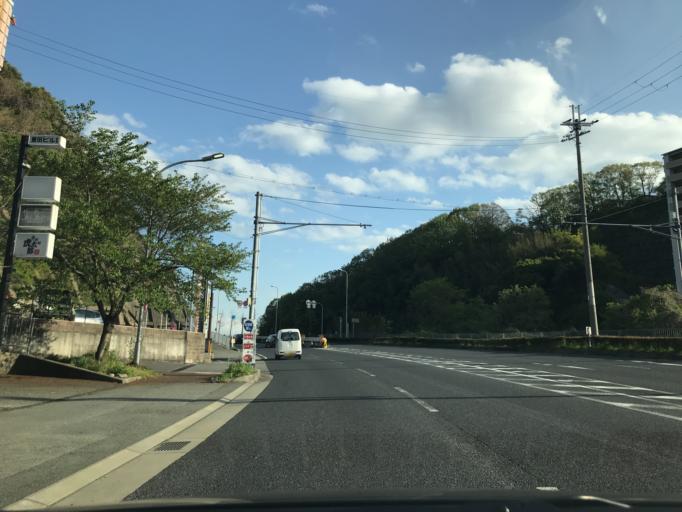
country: JP
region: Osaka
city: Ikeda
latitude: 34.8537
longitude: 135.4168
